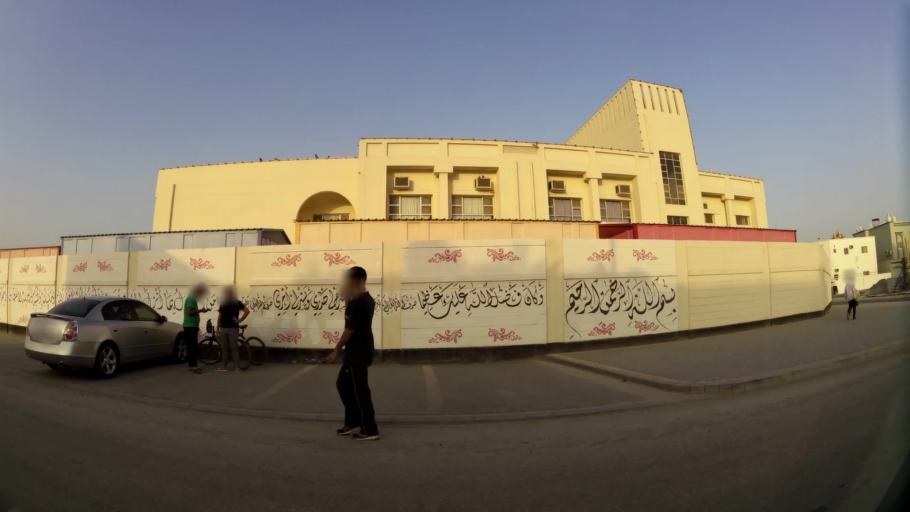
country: BH
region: Northern
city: Madinat `Isa
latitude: 26.1860
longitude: 50.4770
